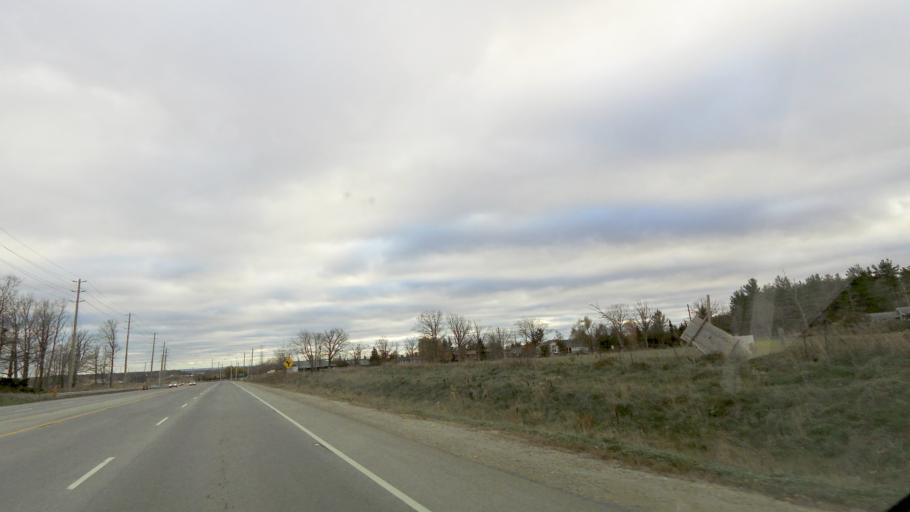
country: CA
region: Ontario
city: Burlington
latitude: 43.4578
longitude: -79.8041
